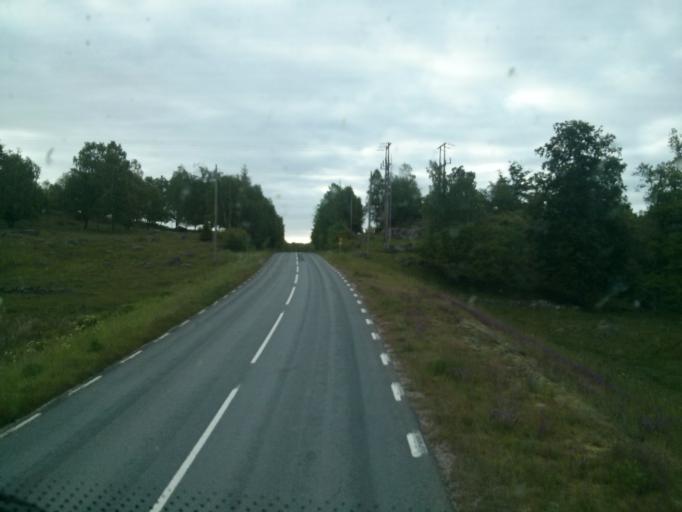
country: SE
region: Blekinge
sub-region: Ronneby Kommun
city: Kallinge
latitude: 56.2848
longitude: 15.2217
